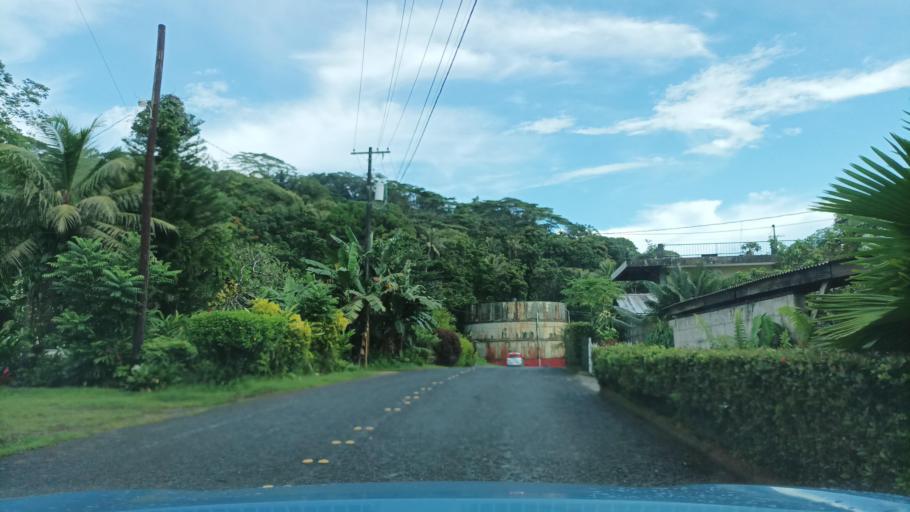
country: FM
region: Pohnpei
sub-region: Kolonia Municipality
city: Kolonia Town
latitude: 6.9502
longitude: 158.2010
